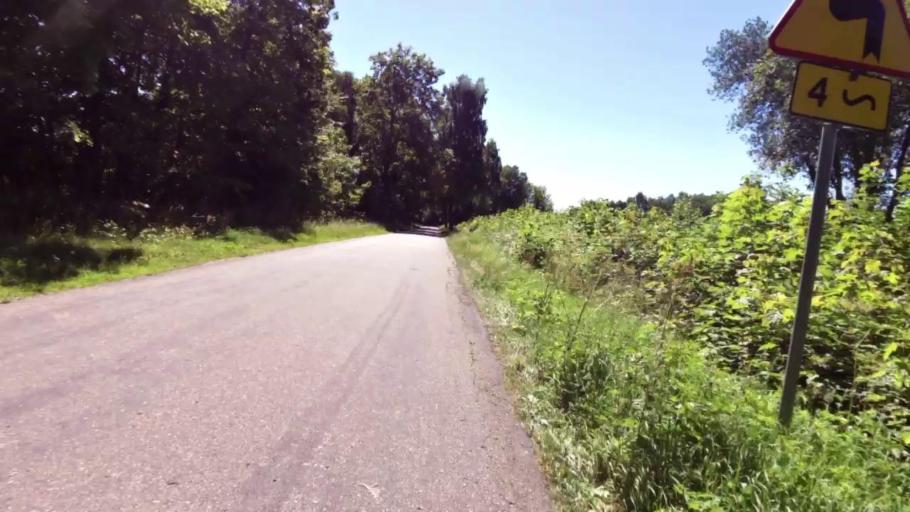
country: PL
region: West Pomeranian Voivodeship
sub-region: Powiat szczecinecki
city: Bialy Bor
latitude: 53.9709
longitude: 16.8648
